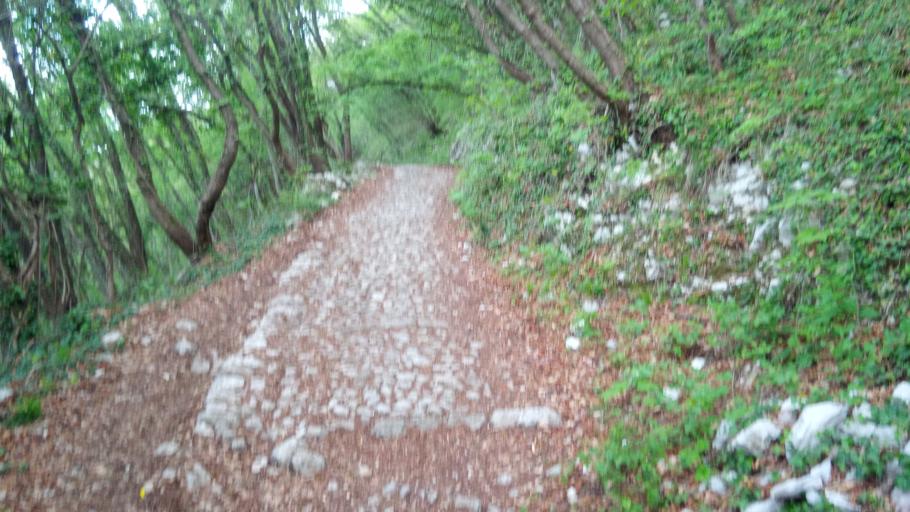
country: IT
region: Veneto
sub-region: Provincia di Vicenza
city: Conco
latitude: 45.7787
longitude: 11.6070
